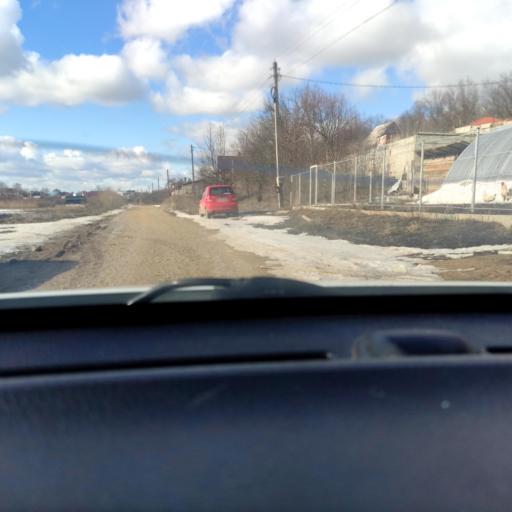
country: RU
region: Voronezj
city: Novaya Usman'
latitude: 51.6881
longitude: 39.3866
